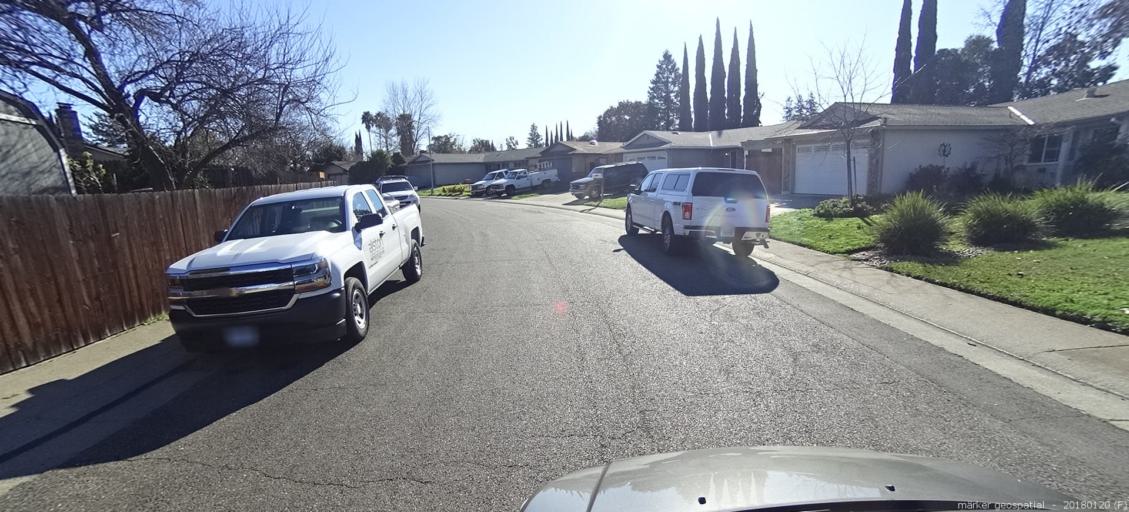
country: US
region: California
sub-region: Sacramento County
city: Rancho Cordova
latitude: 38.5720
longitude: -121.3110
